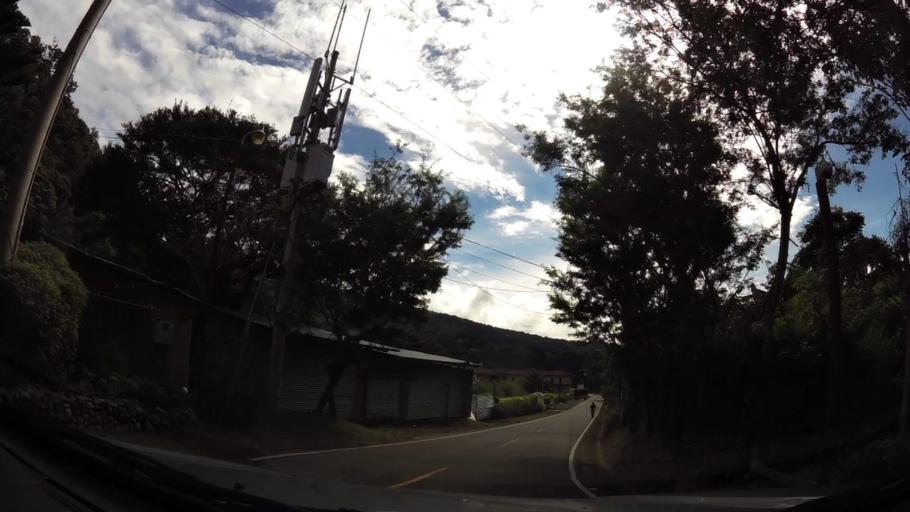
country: PA
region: Chiriqui
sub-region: Distrito Boquete
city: Boquete
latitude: 8.7777
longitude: -82.4390
